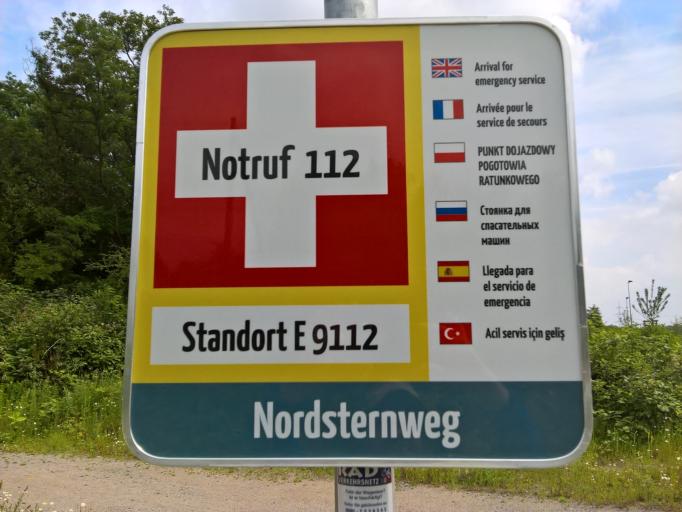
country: DE
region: North Rhine-Westphalia
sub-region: Regierungsbezirk Dusseldorf
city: Essen
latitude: 51.5077
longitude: 7.0402
